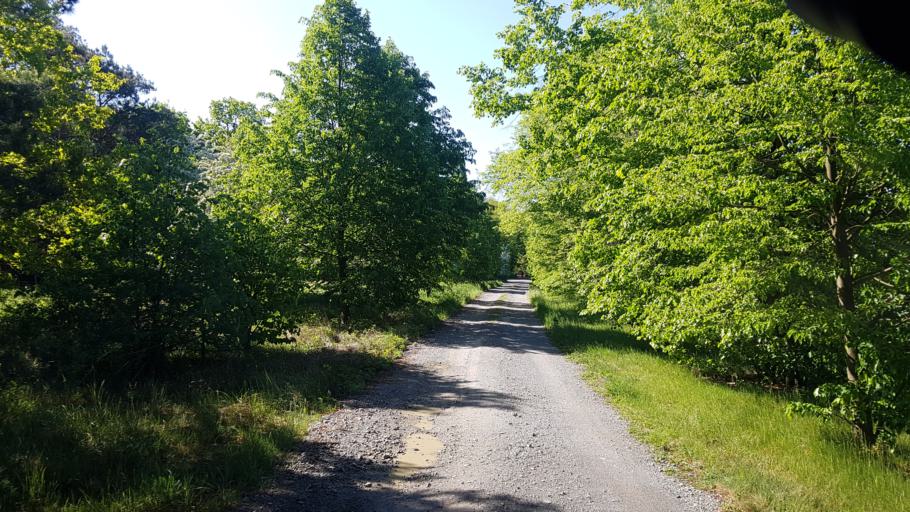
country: DE
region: Brandenburg
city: Grossraschen
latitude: 51.5877
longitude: 13.9623
